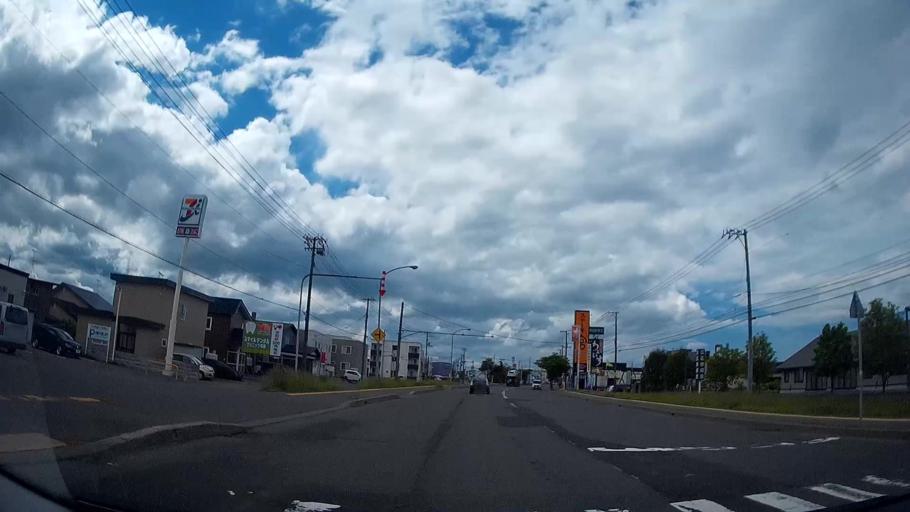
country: JP
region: Hokkaido
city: Chitose
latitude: 42.8716
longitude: 141.5866
